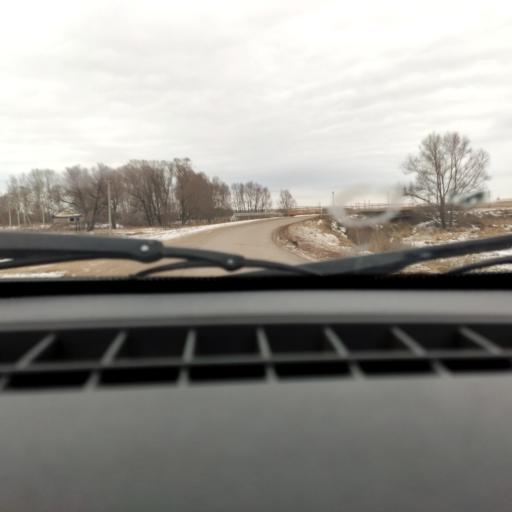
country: RU
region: Bashkortostan
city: Tolbazy
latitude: 54.2528
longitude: 55.9170
